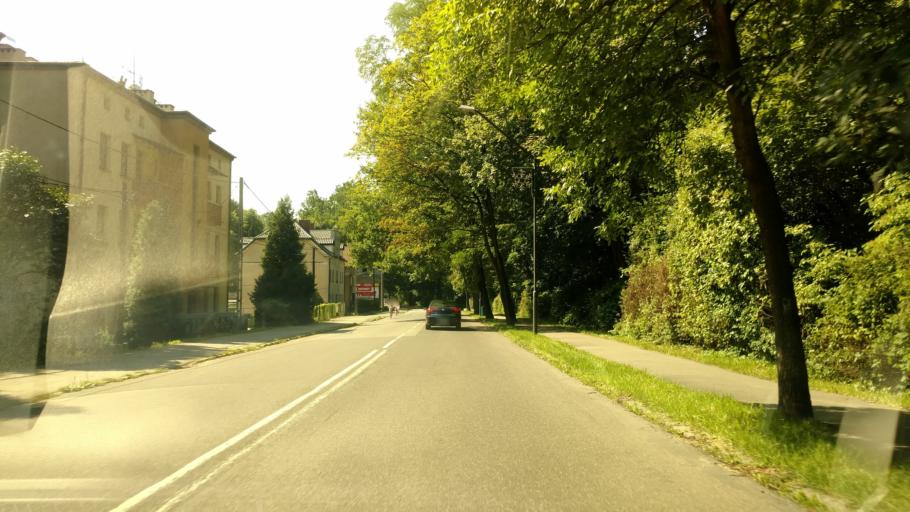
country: PL
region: Silesian Voivodeship
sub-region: Powiat pszczynski
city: Pszczyna
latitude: 49.9819
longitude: 18.9463
